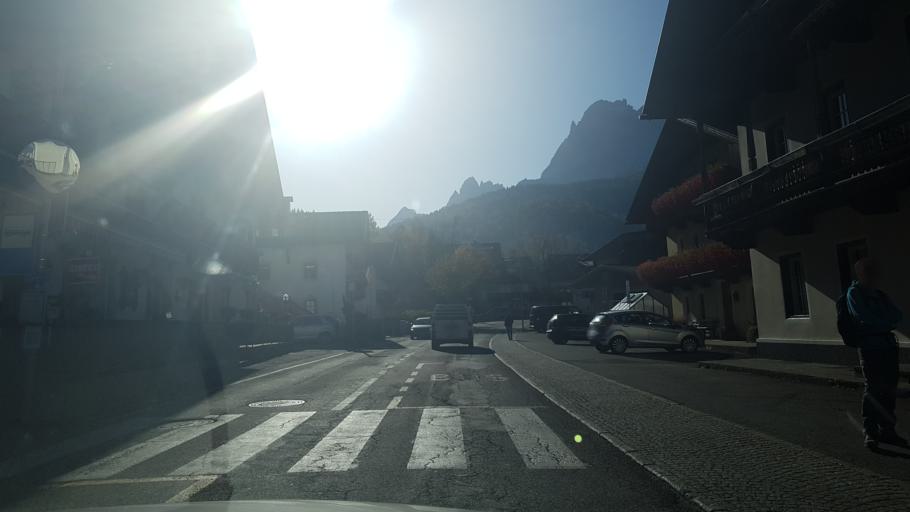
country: IT
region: Trentino-Alto Adige
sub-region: Bolzano
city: Sesto
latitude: 46.6896
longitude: 12.3668
